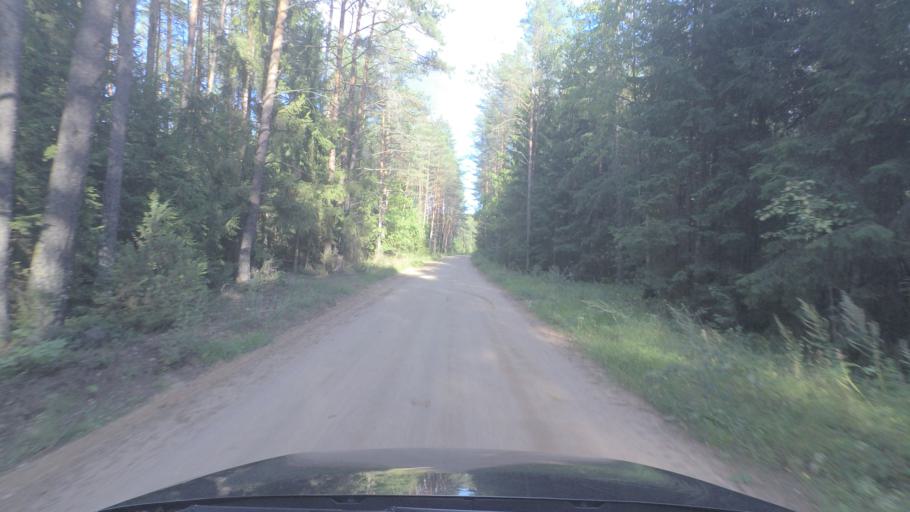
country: LT
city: Pabrade
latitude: 55.1484
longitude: 25.7516
